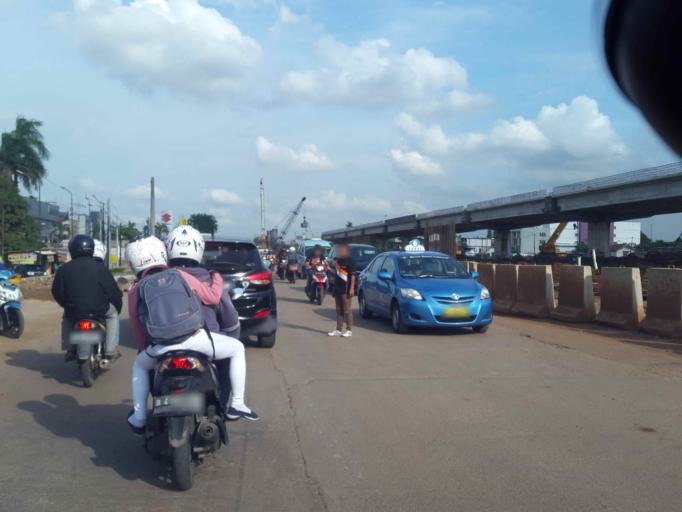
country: ID
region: West Java
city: Bekasi
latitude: -6.2479
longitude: 106.9262
